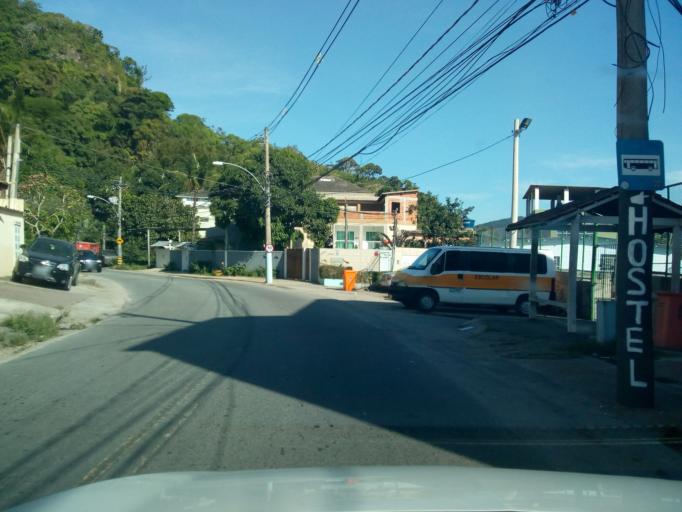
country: BR
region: Rio de Janeiro
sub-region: Nilopolis
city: Nilopolis
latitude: -23.0283
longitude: -43.4994
